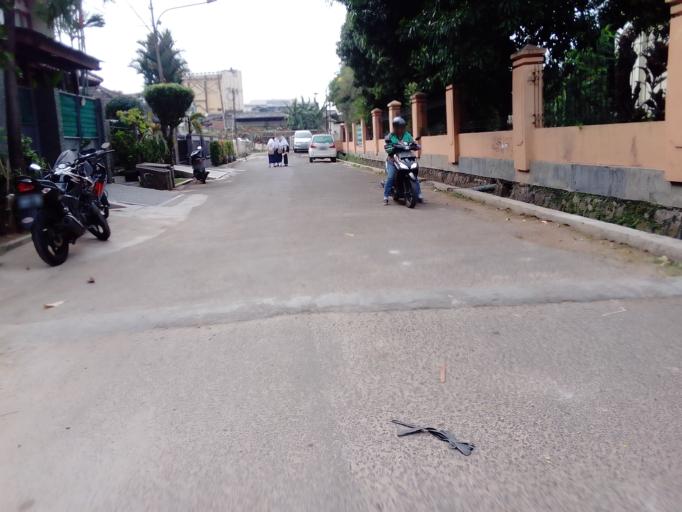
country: ID
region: Jakarta Raya
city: Jakarta
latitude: -6.2002
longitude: 106.8060
